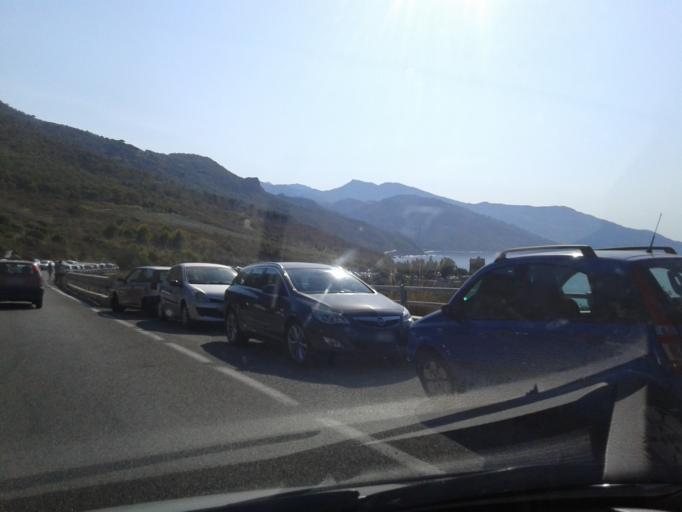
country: IT
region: Sicily
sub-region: Palermo
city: Finale
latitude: 38.0226
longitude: 14.1441
